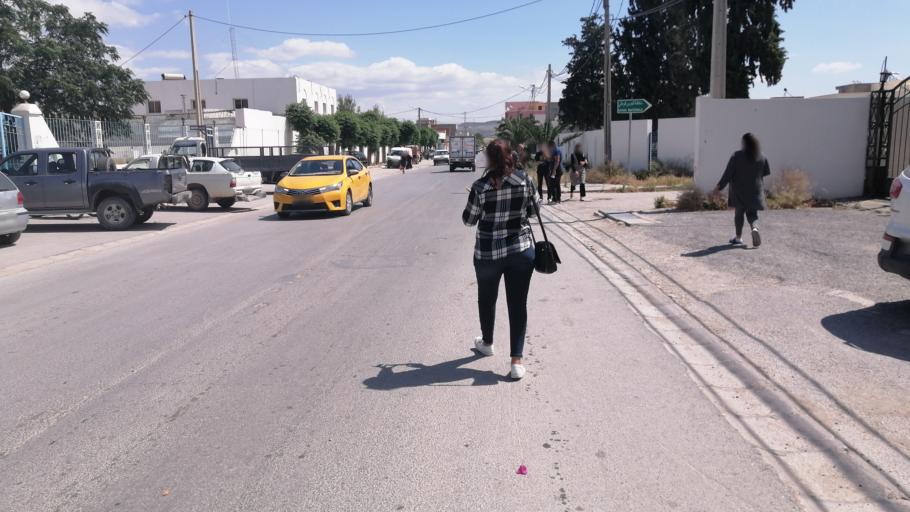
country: TN
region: Silyanah
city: Siliana
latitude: 36.0882
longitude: 9.3738
